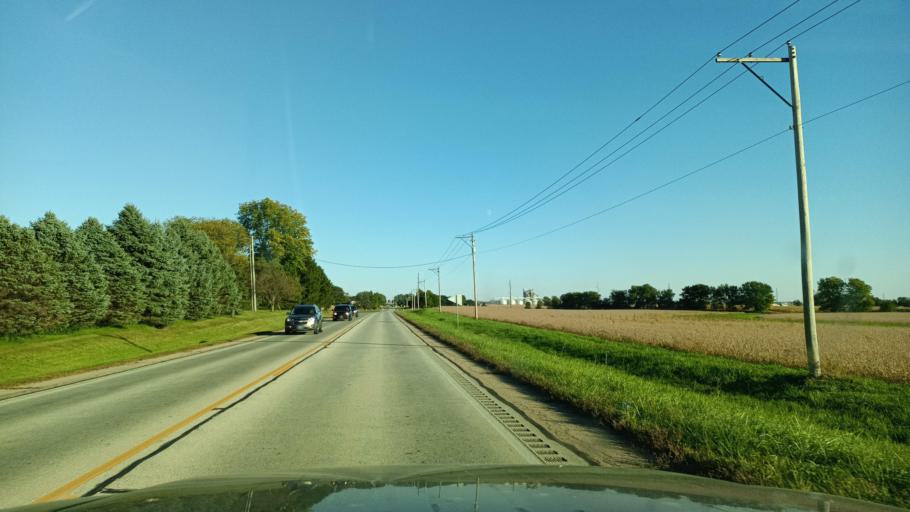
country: US
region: Illinois
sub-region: Champaign County
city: Lake of the Woods
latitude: 40.1739
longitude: -88.3431
